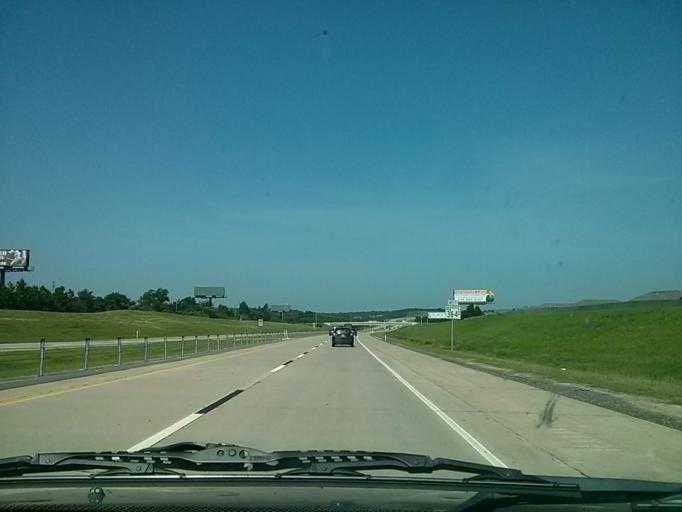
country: US
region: Oklahoma
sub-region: Tulsa County
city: Jenks
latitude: 36.0096
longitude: -96.0205
